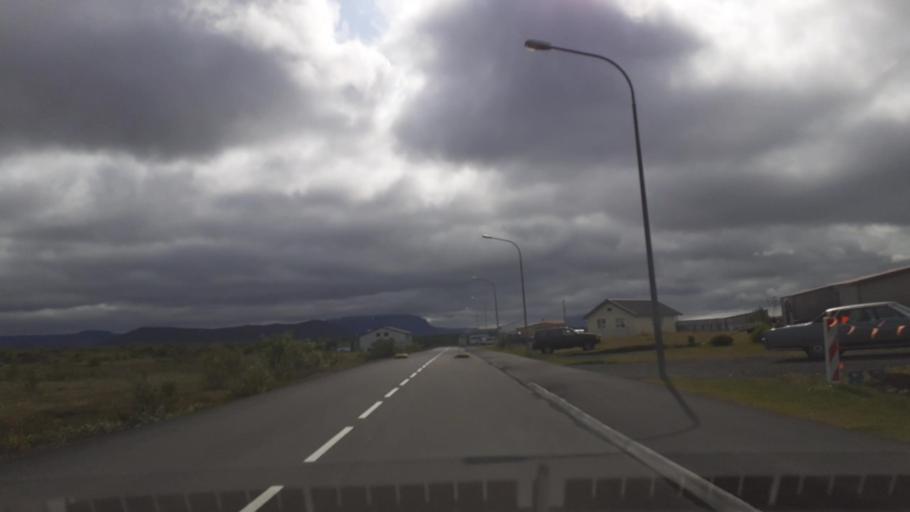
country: IS
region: Northeast
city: Laugar
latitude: 65.6415
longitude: -16.8957
